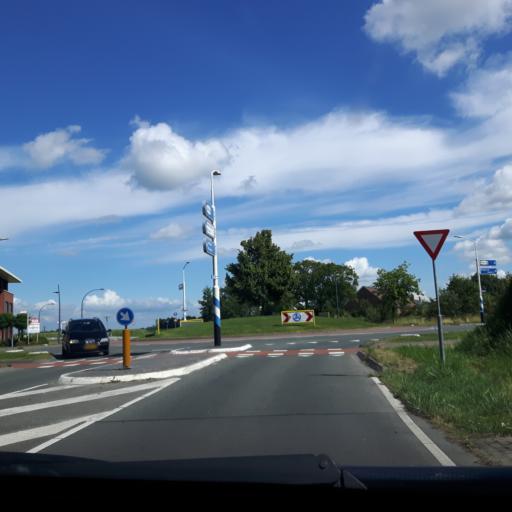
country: NL
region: Zeeland
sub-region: Gemeente Goes
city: Goes
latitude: 51.5108
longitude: 3.9070
